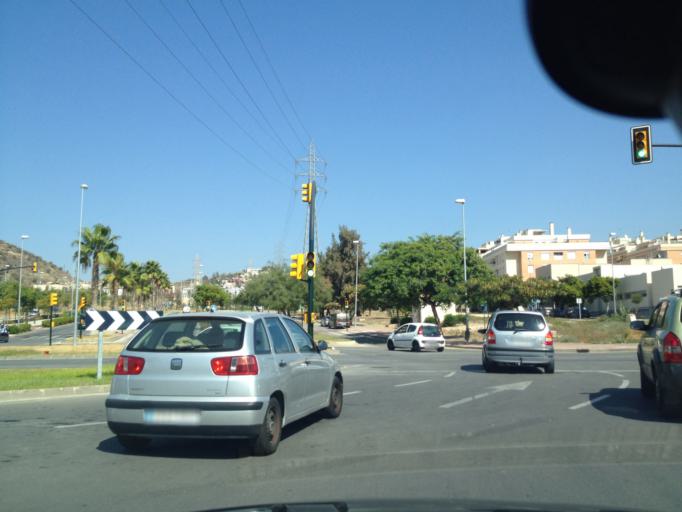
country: ES
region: Andalusia
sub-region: Provincia de Malaga
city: Malaga
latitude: 36.7244
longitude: -4.4706
